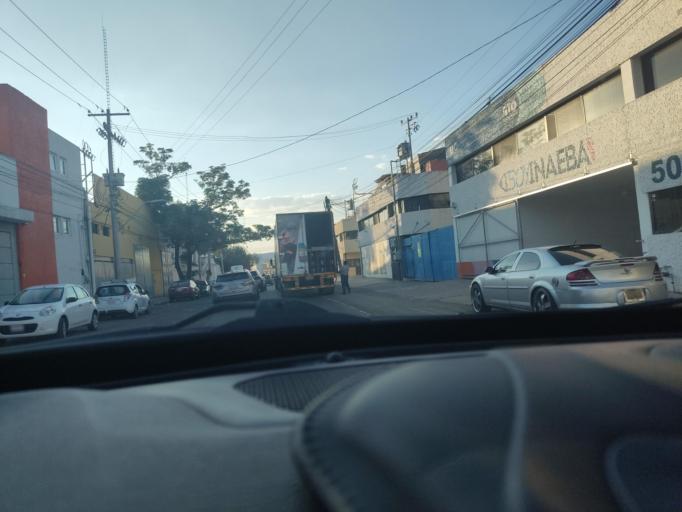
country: MX
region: Guanajuato
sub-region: Leon
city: Fraccionamiento Paraiso Real
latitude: 21.1044
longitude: -101.6248
